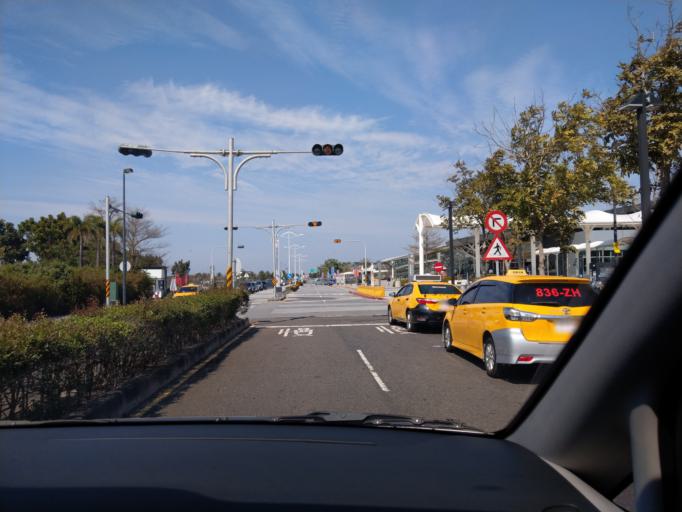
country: TW
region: Taiwan
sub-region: Chiayi
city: Taibao
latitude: 23.4582
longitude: 120.3225
